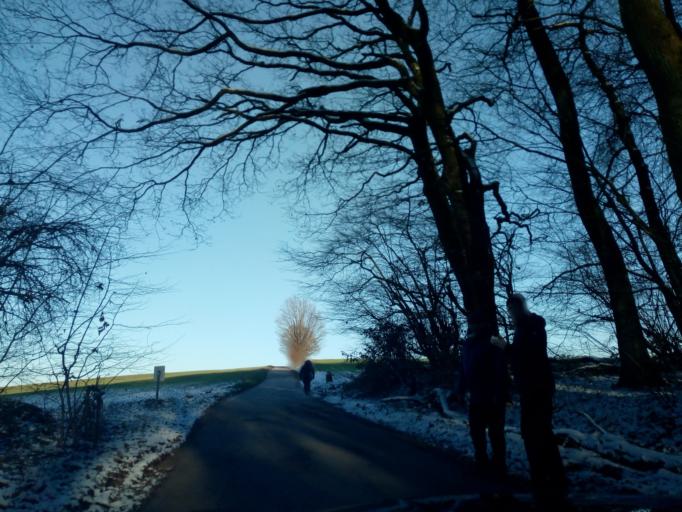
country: DE
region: Saarland
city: Heusweiler
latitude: 49.3637
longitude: 6.9550
